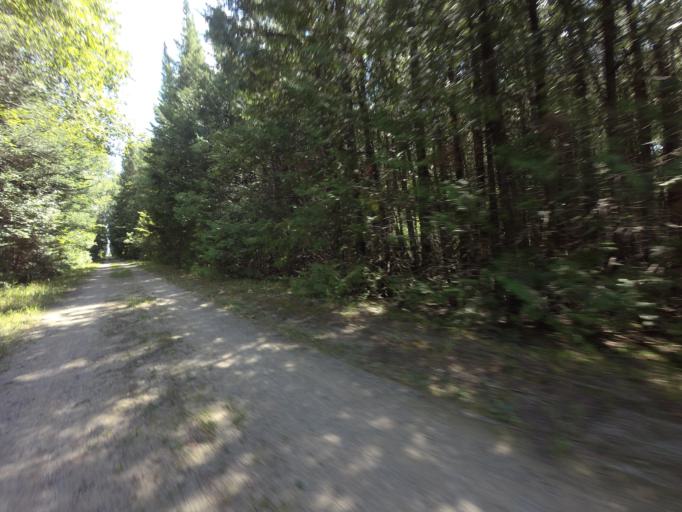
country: CA
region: Ontario
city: Orangeville
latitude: 43.7814
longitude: -80.2196
